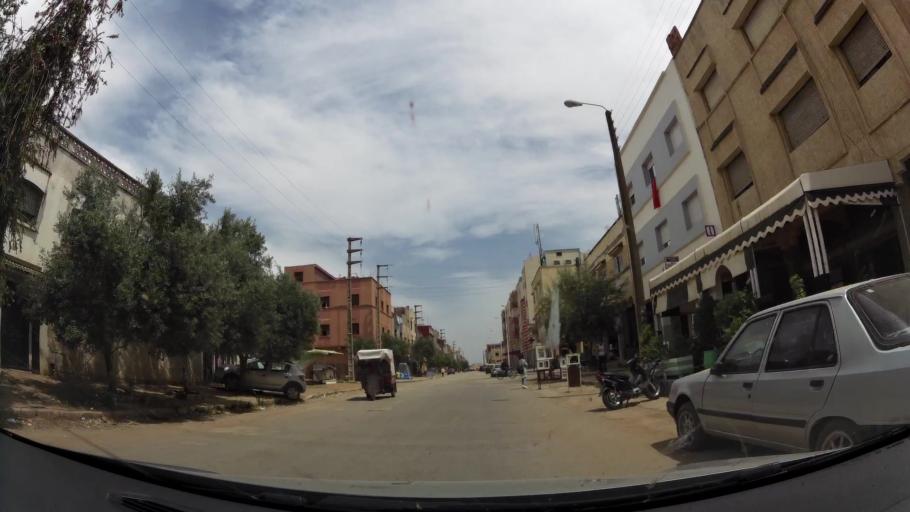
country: MA
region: Rabat-Sale-Zemmour-Zaer
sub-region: Khemisset
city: Khemisset
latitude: 33.8153
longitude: -6.0711
